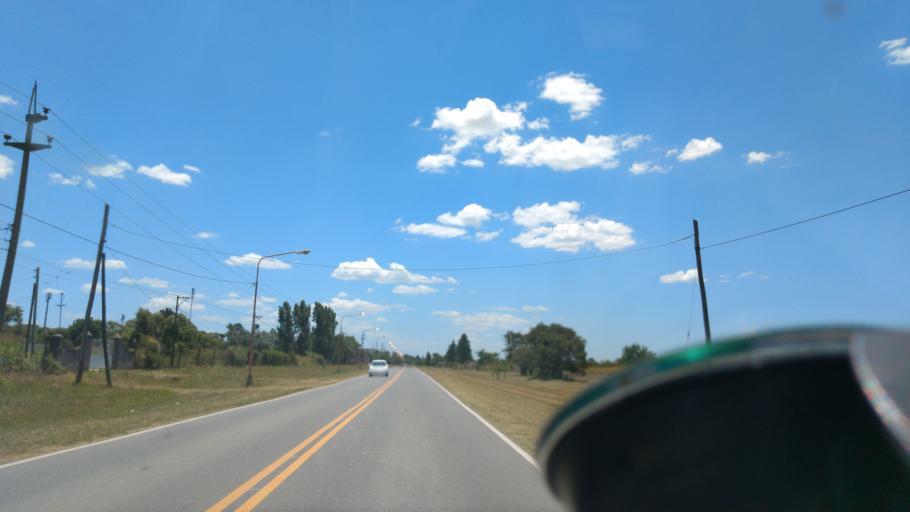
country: AR
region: Santa Fe
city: Laguna Paiva
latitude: -31.3242
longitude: -60.6590
